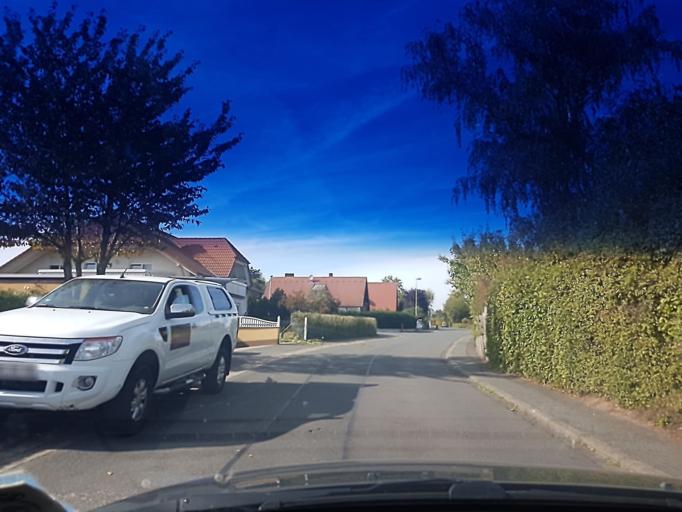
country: DE
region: Bavaria
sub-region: Upper Franconia
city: Schlusselfeld
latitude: 49.7644
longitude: 10.6185
